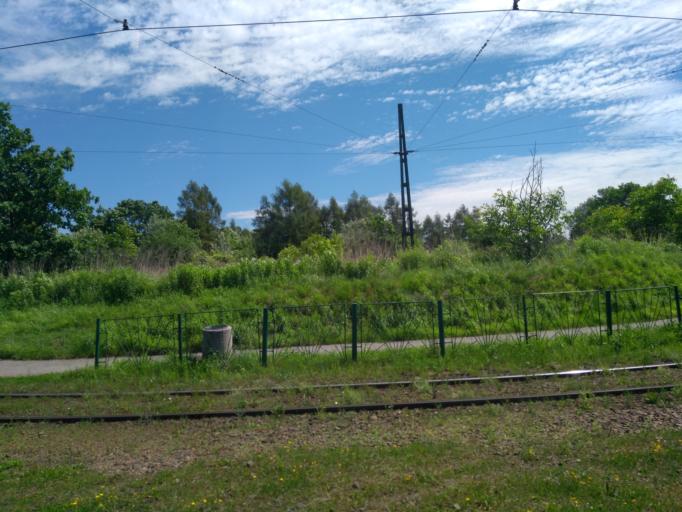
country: PL
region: Lesser Poland Voivodeship
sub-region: Powiat wielicki
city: Kokotow
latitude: 50.0880
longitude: 20.0566
